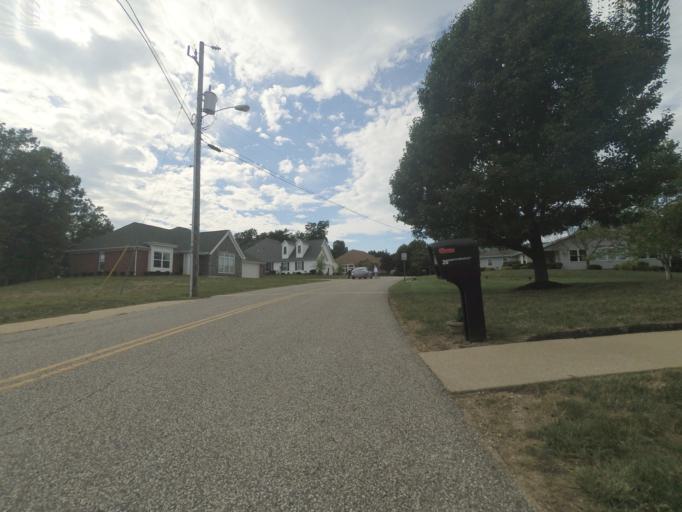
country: US
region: West Virginia
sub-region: Cabell County
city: Huntington
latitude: 38.3931
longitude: -82.4632
